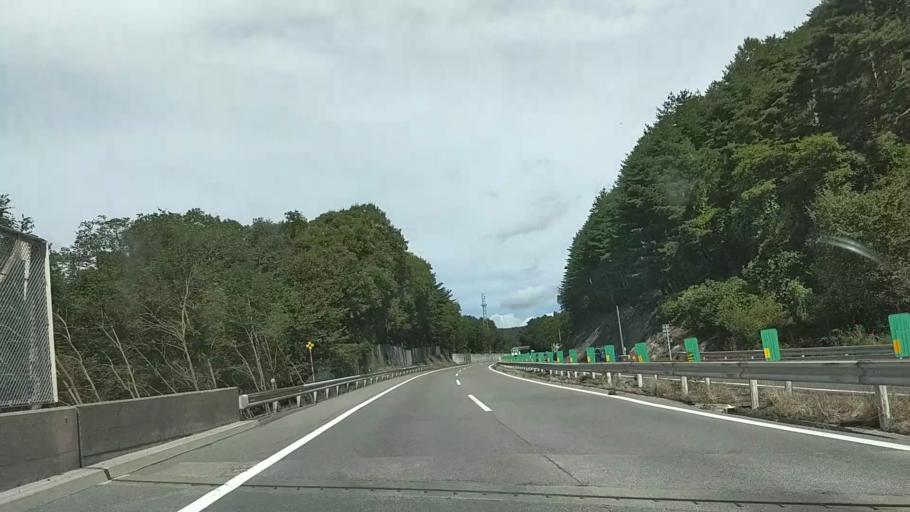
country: JP
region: Nagano
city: Chino
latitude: 35.8737
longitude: 138.3066
